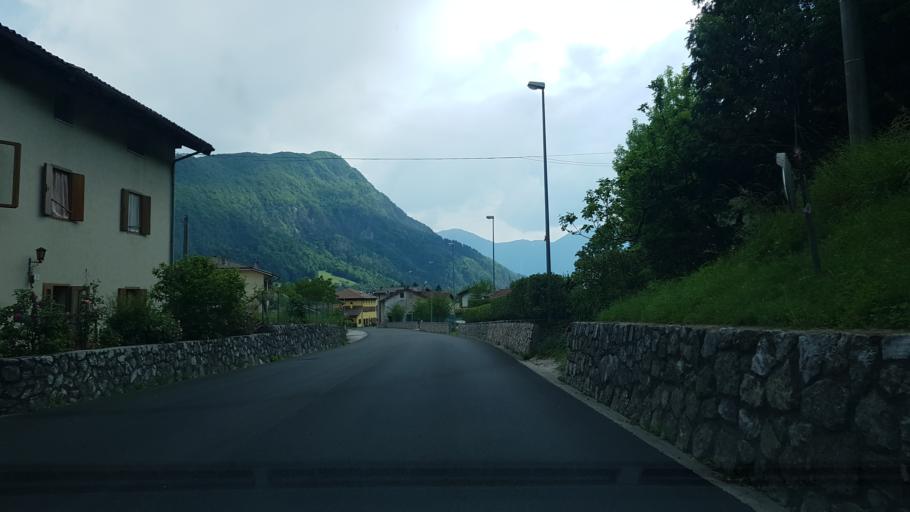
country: IT
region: Friuli Venezia Giulia
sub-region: Provincia di Udine
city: Zuglio
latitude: 46.4442
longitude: 13.0323
